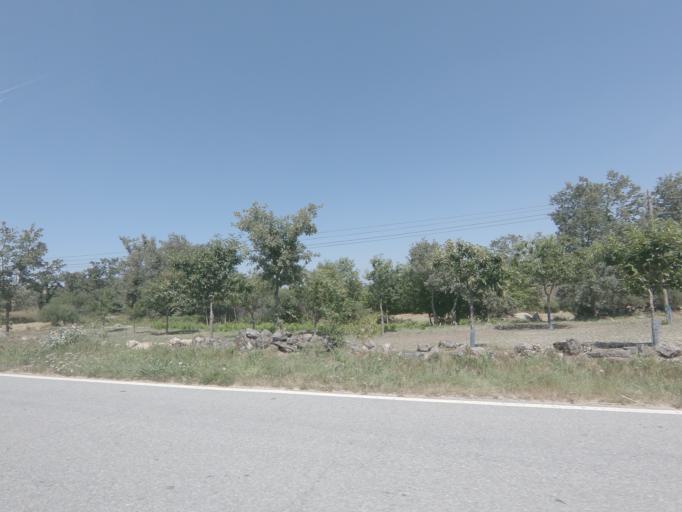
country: PT
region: Viseu
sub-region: Tarouca
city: Tarouca
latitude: 41.0012
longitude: -7.8872
